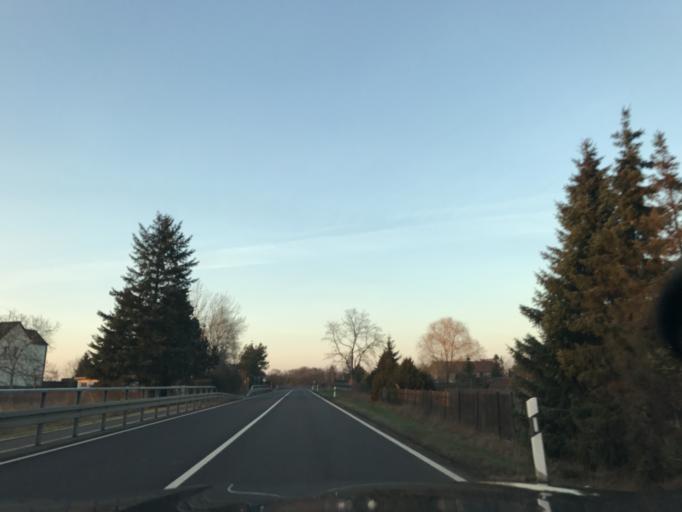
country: DE
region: Brandenburg
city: Brandenburg an der Havel
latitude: 52.4863
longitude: 12.4640
